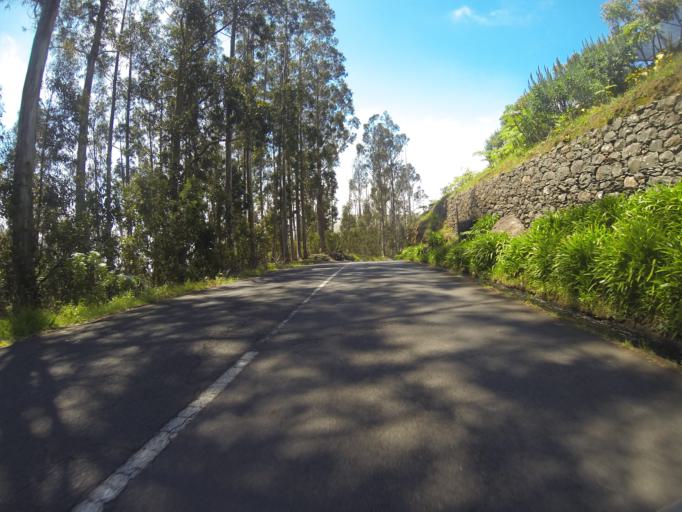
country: PT
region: Madeira
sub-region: Funchal
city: Nossa Senhora do Monte
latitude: 32.6938
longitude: -16.9015
